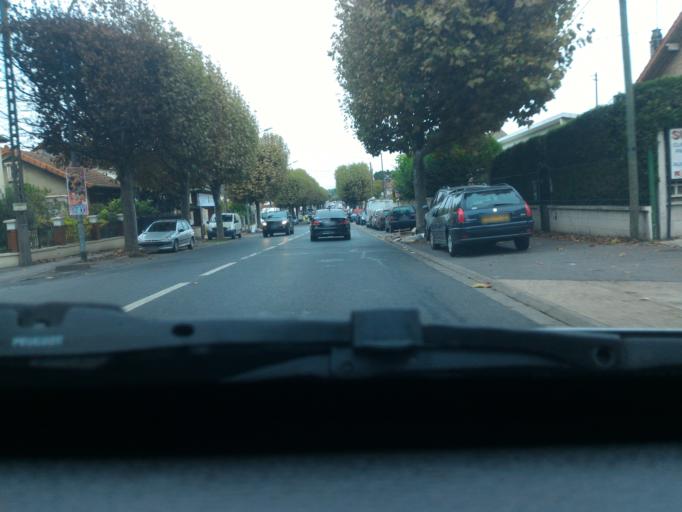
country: FR
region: Ile-de-France
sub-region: Departement du Val-de-Marne
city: Boissy-Saint-Leger
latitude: 48.7755
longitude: 2.5112
